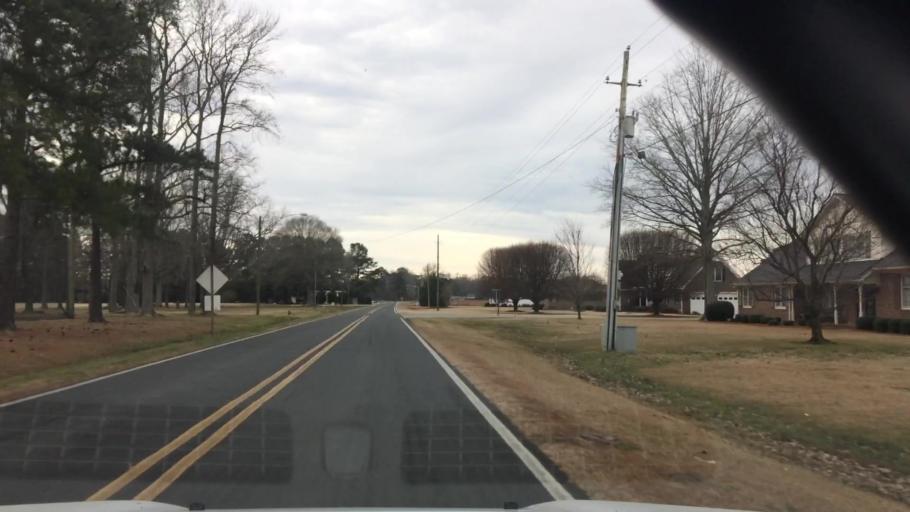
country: US
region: North Carolina
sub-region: Pitt County
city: Ayden
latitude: 35.4613
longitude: -77.3908
